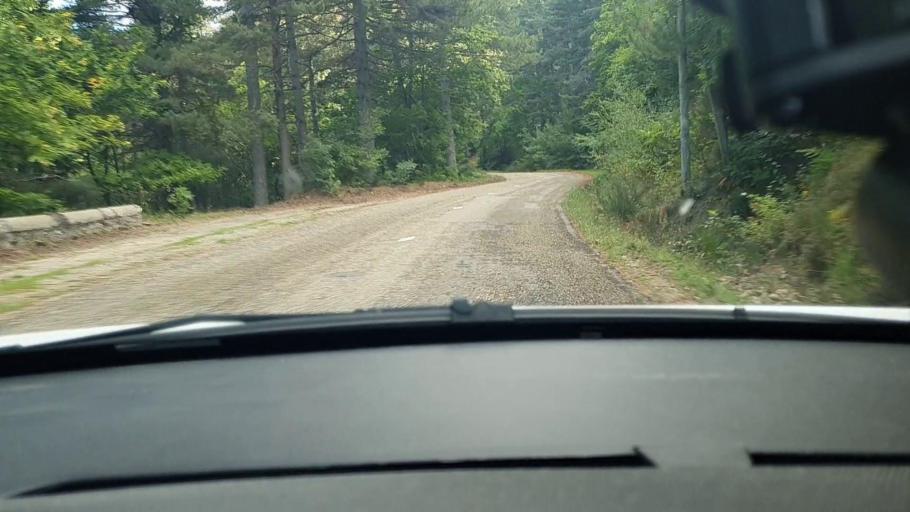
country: FR
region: Rhone-Alpes
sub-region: Departement de l'Ardeche
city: Les Vans
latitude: 44.3992
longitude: 3.9995
